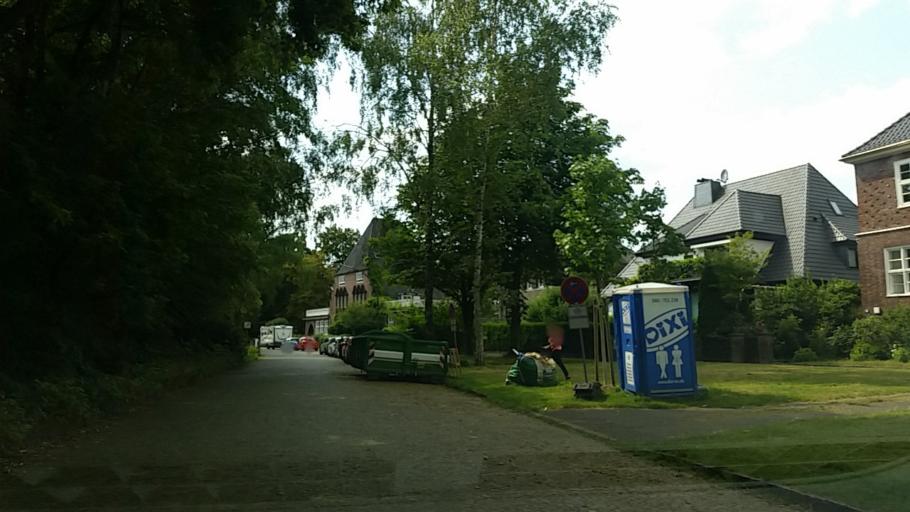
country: DE
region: Hamburg
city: Alsterdorf
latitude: 53.6125
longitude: 10.0023
